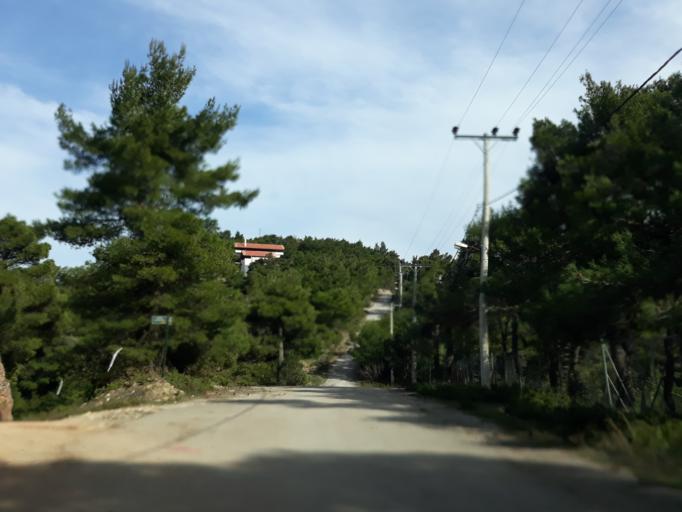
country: GR
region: Attica
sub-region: Nomarchia Anatolikis Attikis
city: Afidnes
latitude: 38.2171
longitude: 23.8004
